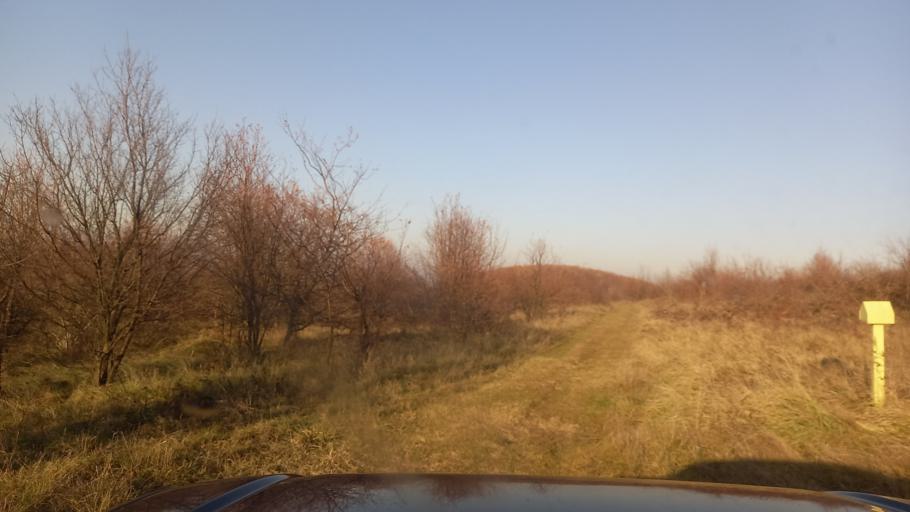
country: RU
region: Krasnodarskiy
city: Azovskaya
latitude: 44.8100
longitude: 38.5949
